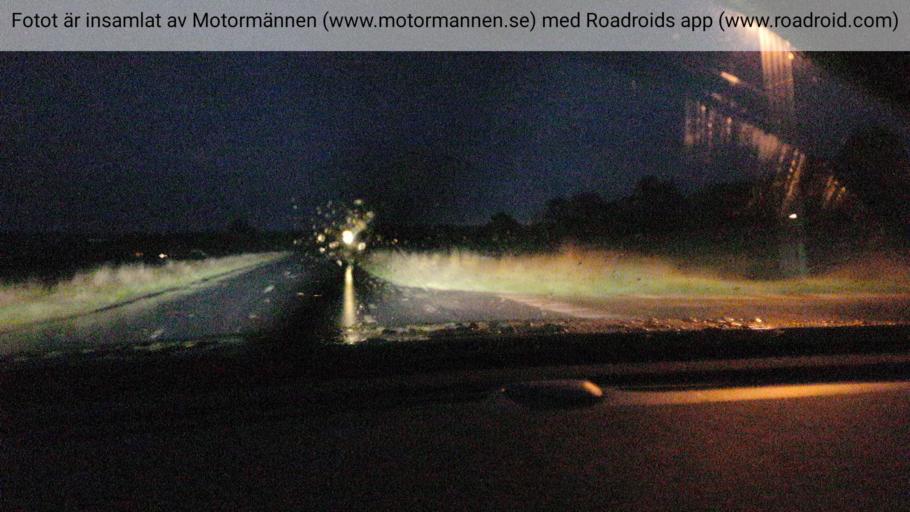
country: SE
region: Vaestra Goetaland
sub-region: Falkopings Kommun
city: Akarp
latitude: 58.3191
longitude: 13.7153
